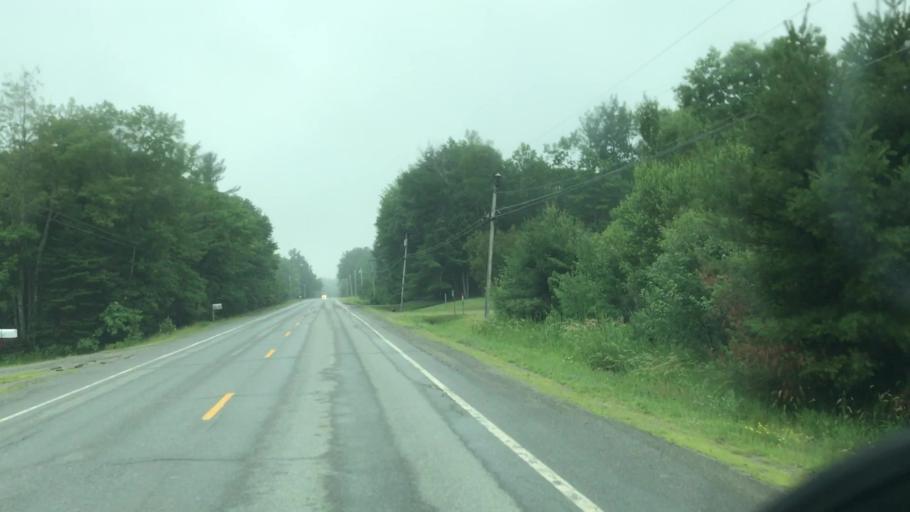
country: US
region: Maine
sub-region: Penobscot County
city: Howland
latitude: 45.2645
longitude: -68.6385
